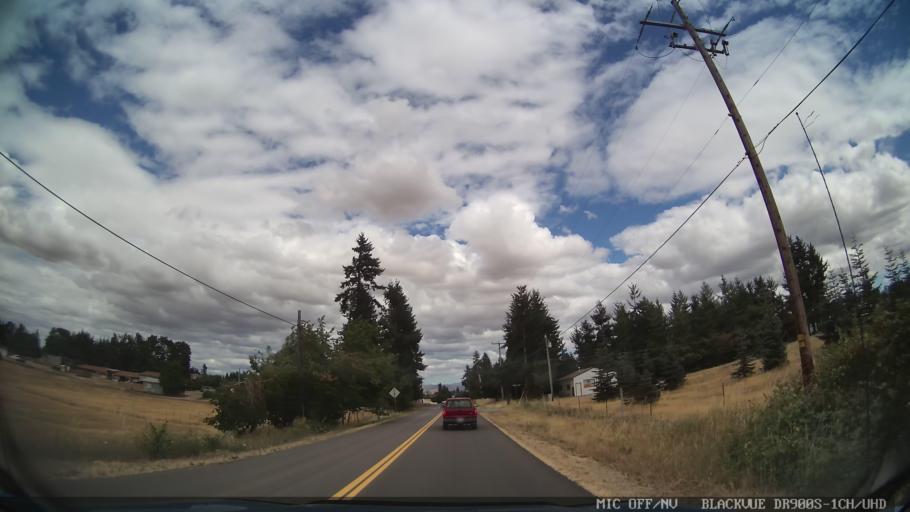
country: US
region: Oregon
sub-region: Marion County
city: Aumsville
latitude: 44.8604
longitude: -122.8603
